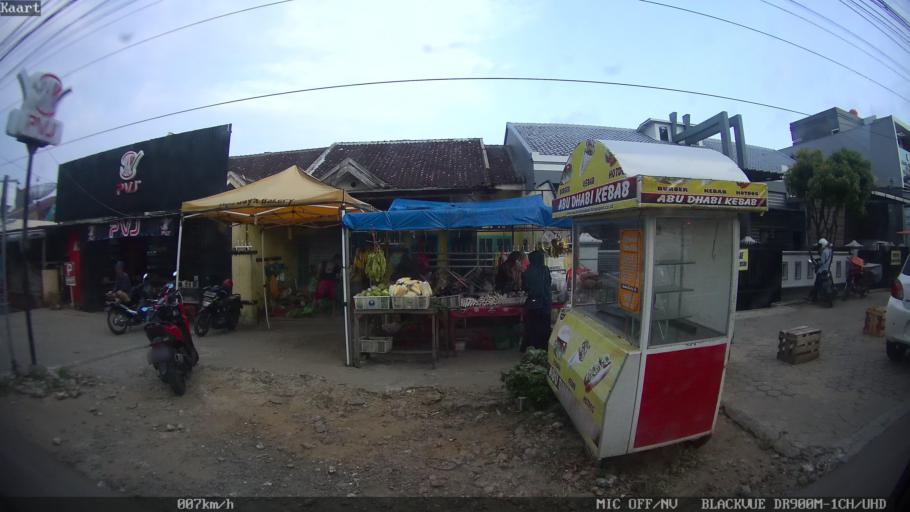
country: ID
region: Lampung
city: Kedaton
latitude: -5.3992
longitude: 105.2119
